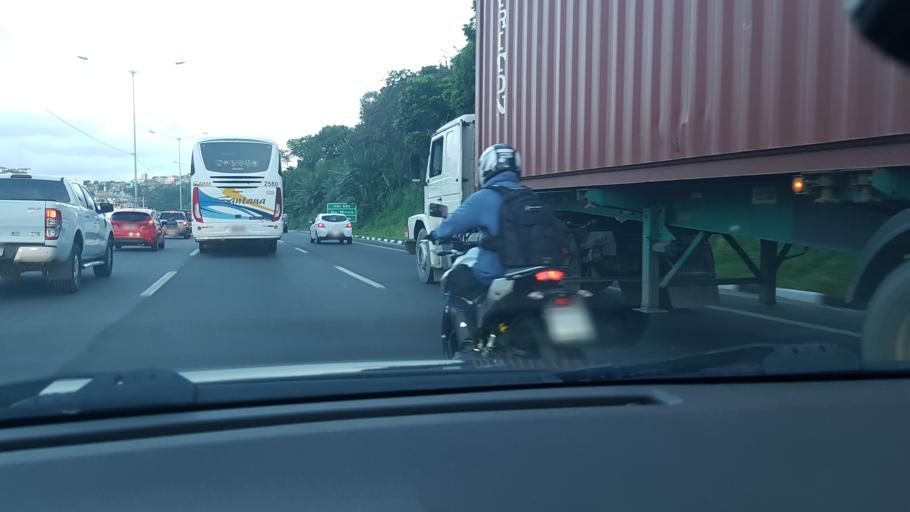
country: BR
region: Bahia
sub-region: Salvador
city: Salvador
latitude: -12.9382
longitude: -38.4722
